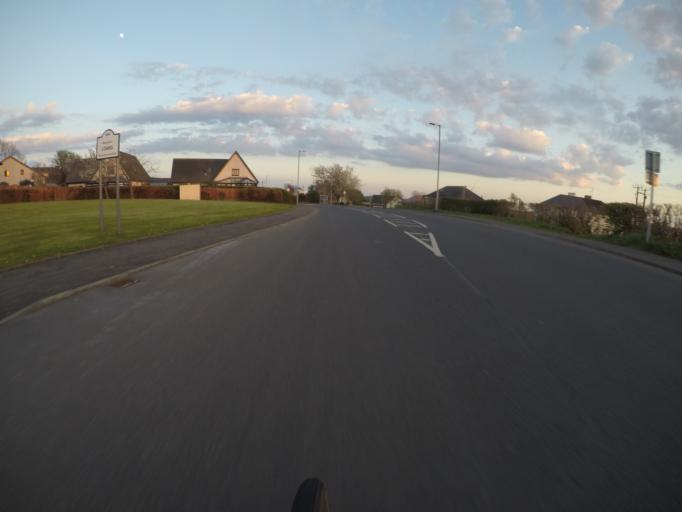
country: GB
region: Scotland
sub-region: South Ayrshire
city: Troon
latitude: 55.5531
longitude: -4.6264
